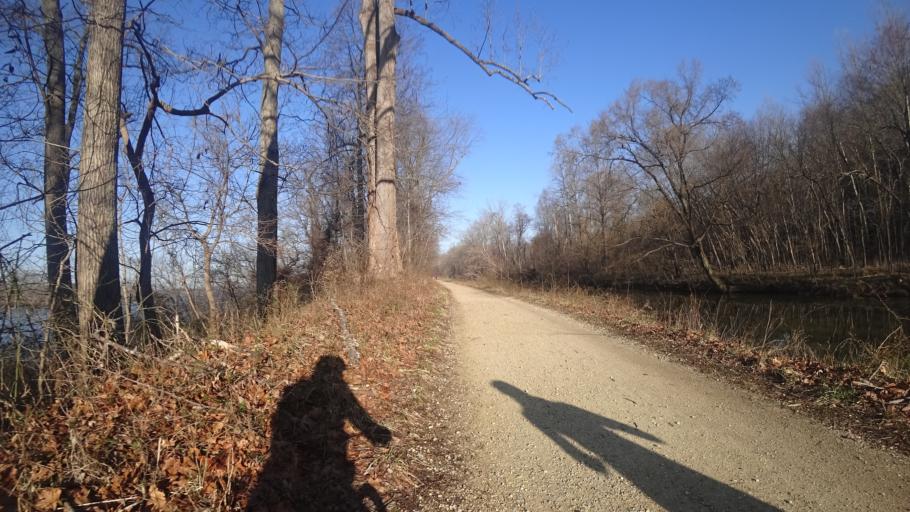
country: US
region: Virginia
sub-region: Loudoun County
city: Lowes Island
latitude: 39.0636
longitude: -77.3201
